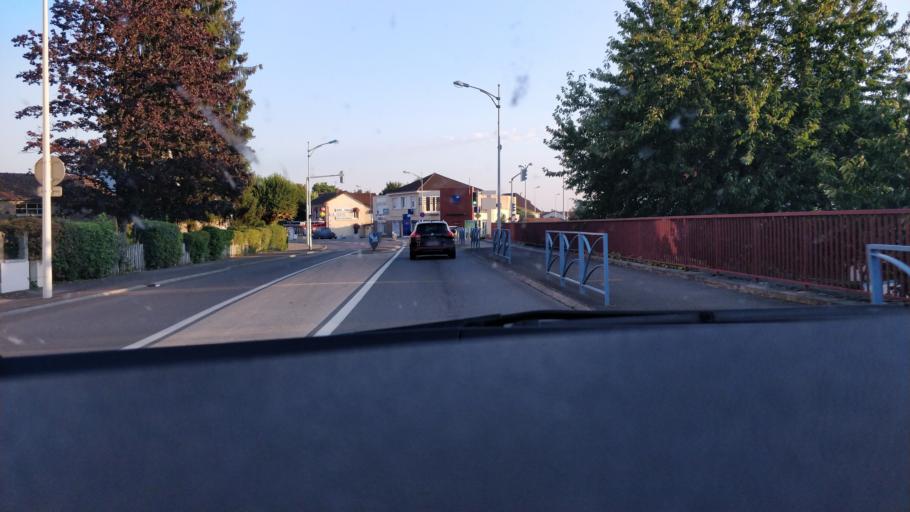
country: FR
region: Limousin
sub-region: Departement de la Haute-Vienne
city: Couzeix
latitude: 45.8642
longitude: 1.2380
